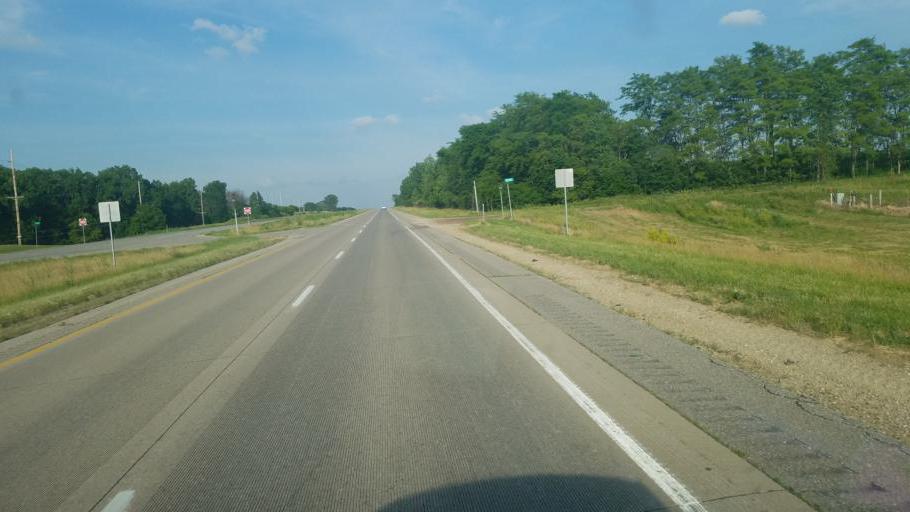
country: US
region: Iowa
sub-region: Marshall County
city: Marshalltown
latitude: 42.0061
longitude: -92.7470
